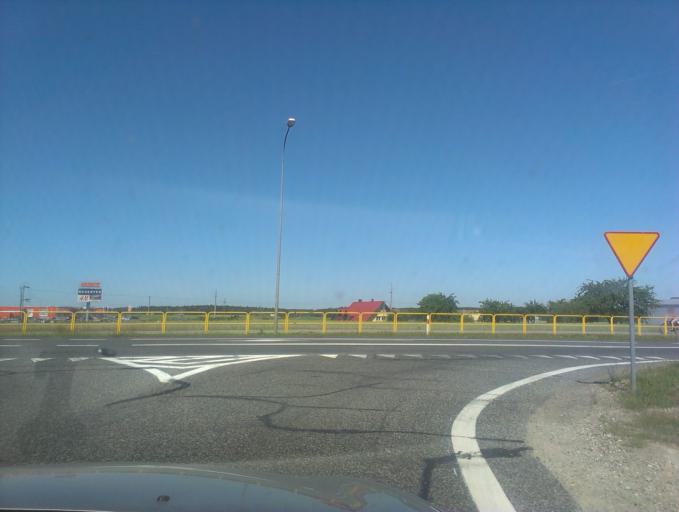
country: PL
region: Pomeranian Voivodeship
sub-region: Powiat chojnicki
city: Chojnice
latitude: 53.6890
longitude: 17.6200
